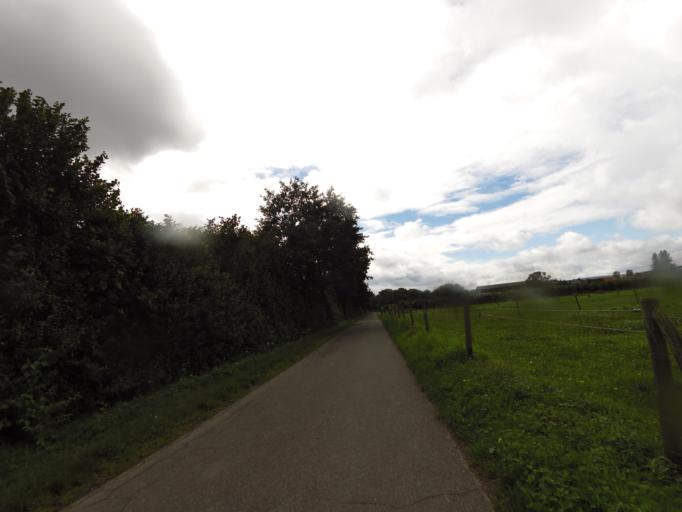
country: DE
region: North Rhine-Westphalia
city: Meckenheim
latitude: 50.5919
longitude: 7.0198
